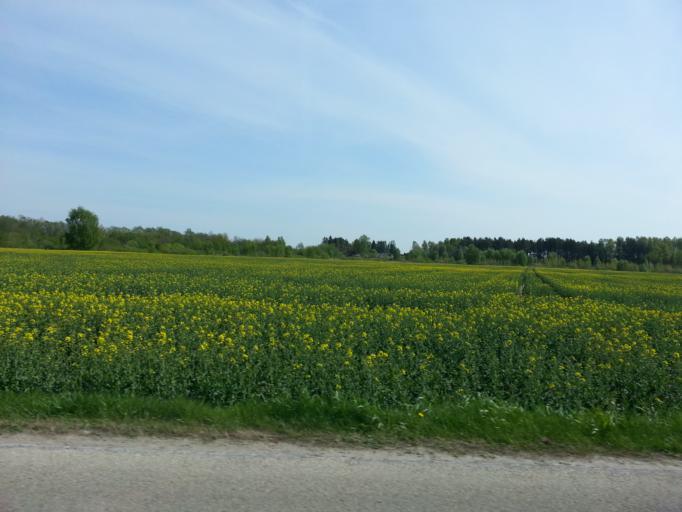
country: LT
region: Panevezys
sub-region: Panevezys City
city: Panevezys
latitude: 55.8052
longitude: 24.2734
